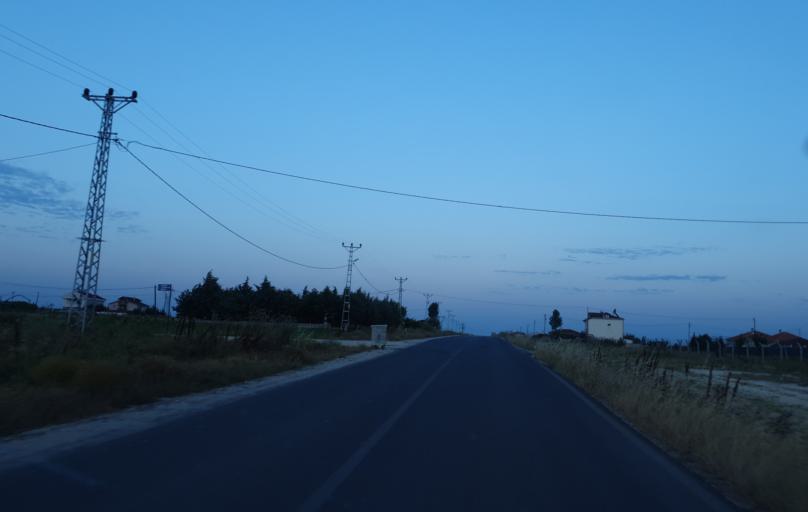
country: TR
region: Tekirdag
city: Velimese
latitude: 41.3428
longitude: 27.8986
